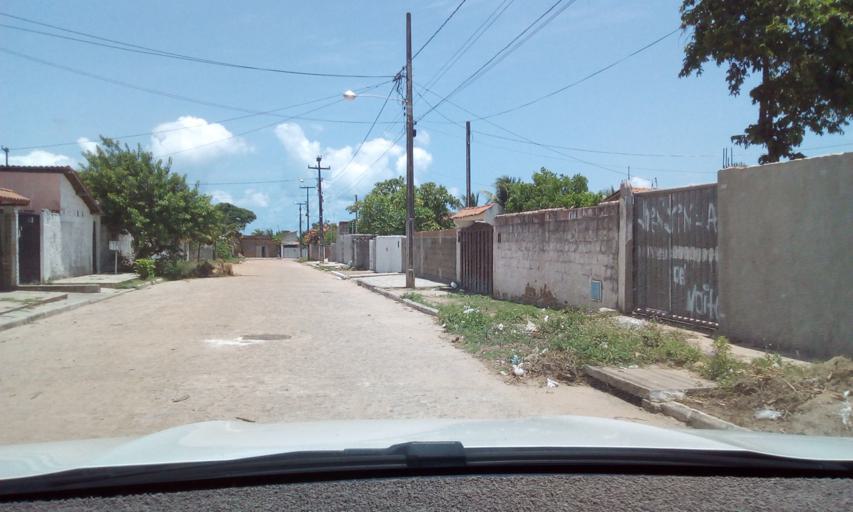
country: BR
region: Paraiba
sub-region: Joao Pessoa
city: Joao Pessoa
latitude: -7.1764
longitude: -34.8161
